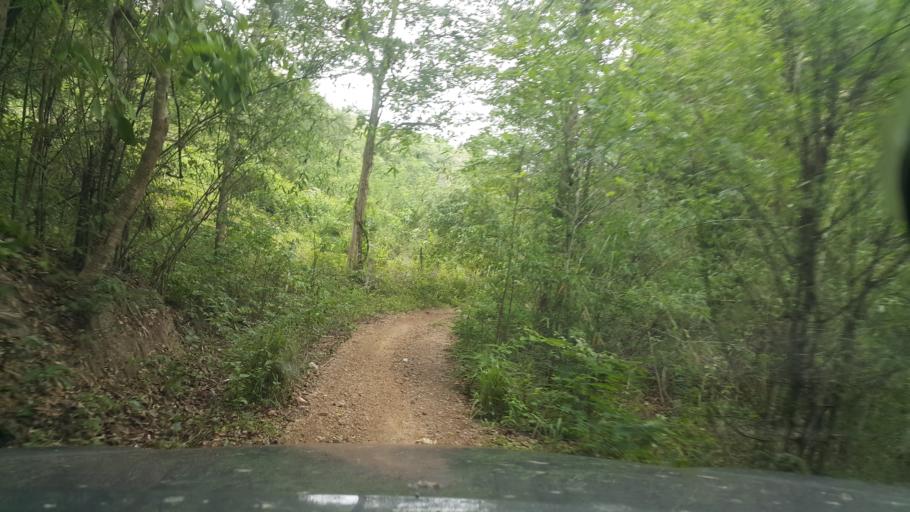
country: TH
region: Chiang Mai
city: Hang Dong
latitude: 18.6913
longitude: 98.8453
